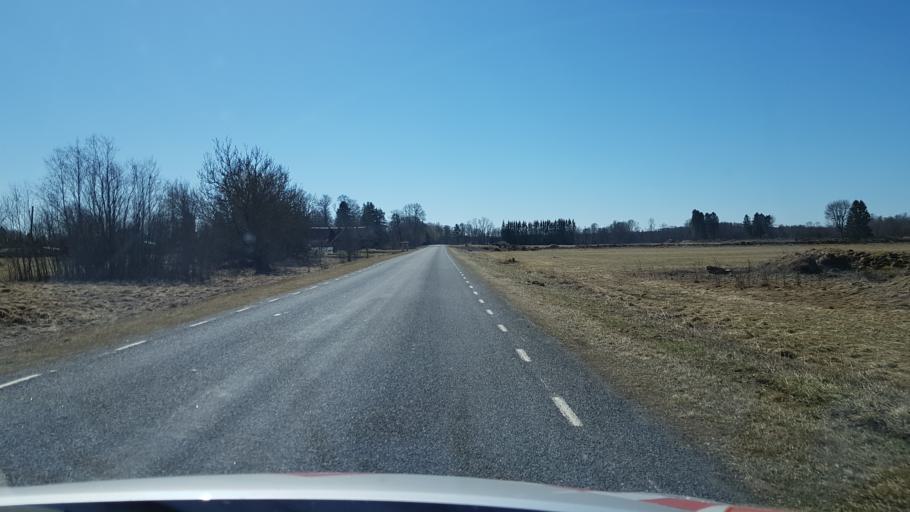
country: EE
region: Laeaene-Virumaa
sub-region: Haljala vald
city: Haljala
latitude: 59.5318
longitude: 26.2360
